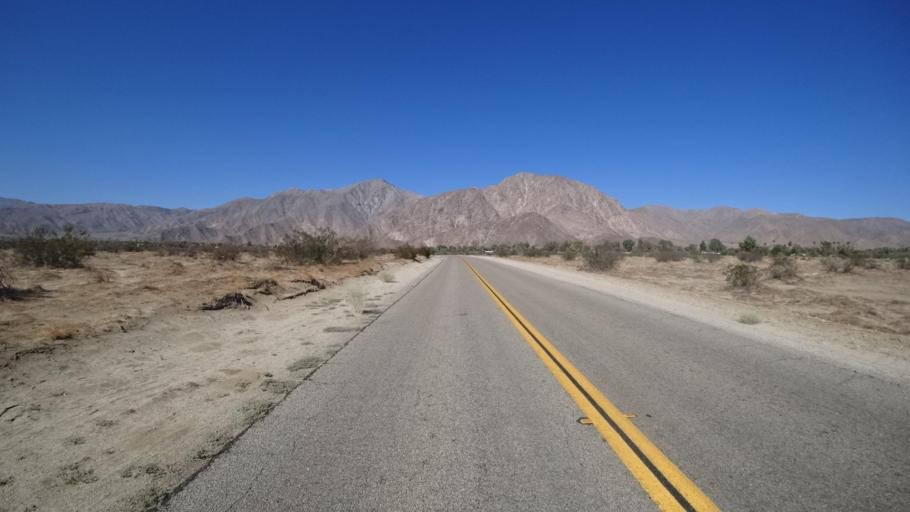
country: US
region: California
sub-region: San Diego County
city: Borrego Springs
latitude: 33.2843
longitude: -116.3803
